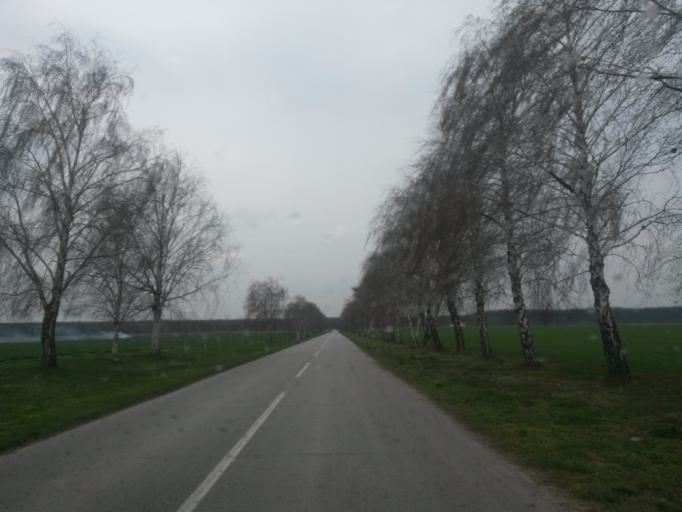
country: HR
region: Vukovarsko-Srijemska
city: Lovas
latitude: 45.2170
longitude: 19.1537
